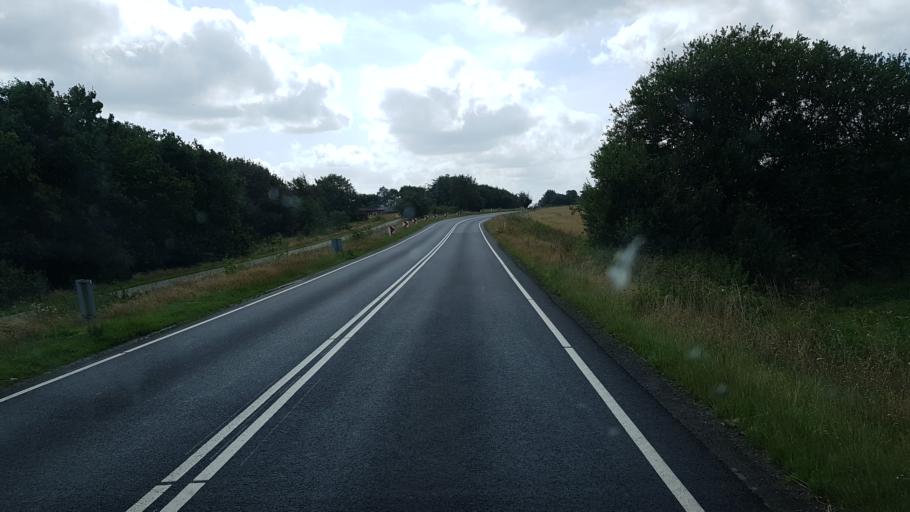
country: DK
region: South Denmark
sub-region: Vejen Kommune
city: Vejen
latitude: 55.5596
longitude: 9.1253
